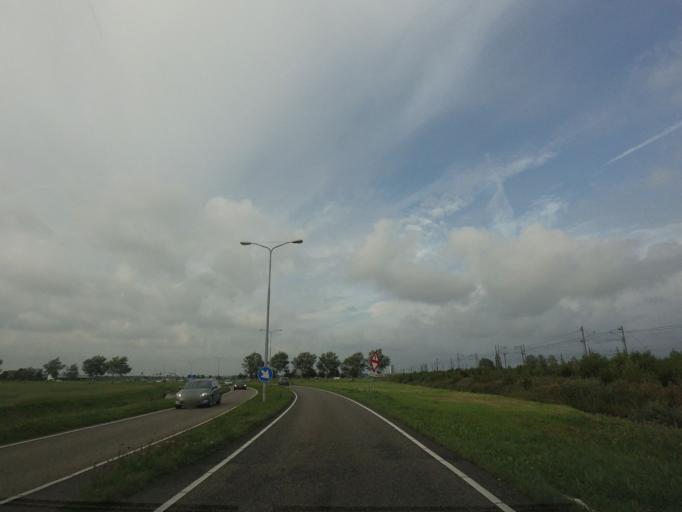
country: NL
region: North Holland
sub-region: Gemeente Haarlemmermeer
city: Hoofddorp
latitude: 52.2772
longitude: 4.6705
